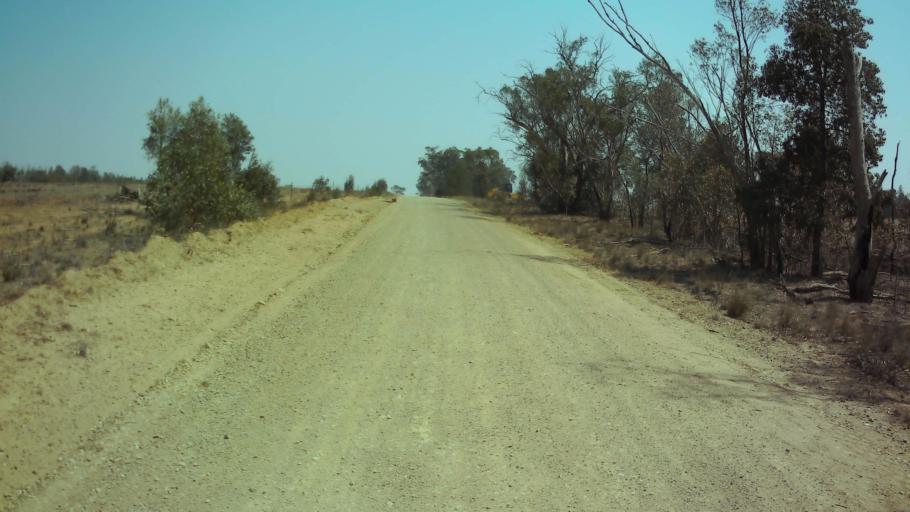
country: AU
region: New South Wales
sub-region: Weddin
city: Grenfell
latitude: -33.6573
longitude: 148.2741
